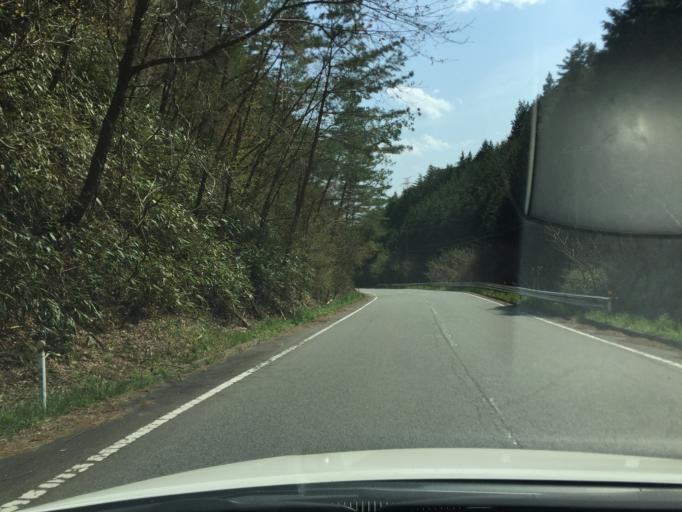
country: JP
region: Fukushima
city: Namie
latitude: 37.3812
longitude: 140.8014
